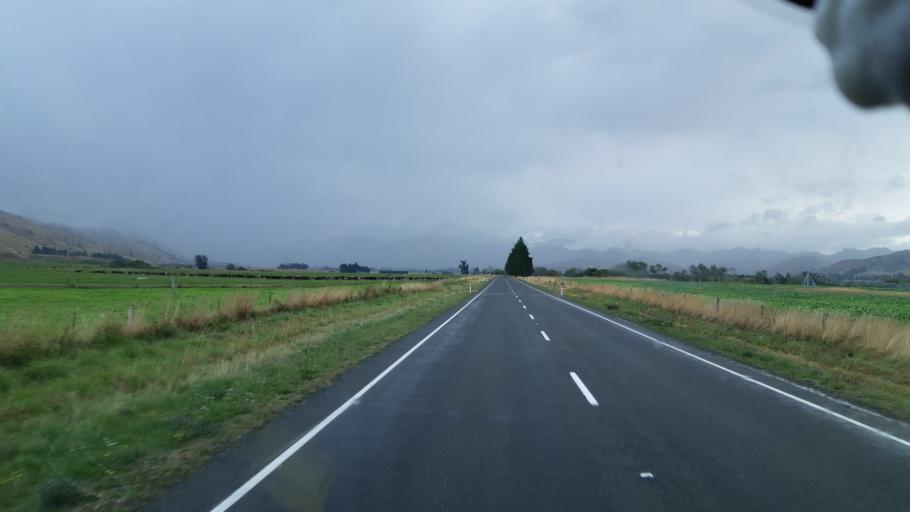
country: NZ
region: Canterbury
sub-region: Hurunui District
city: Amberley
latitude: -42.7104
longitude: 172.8517
